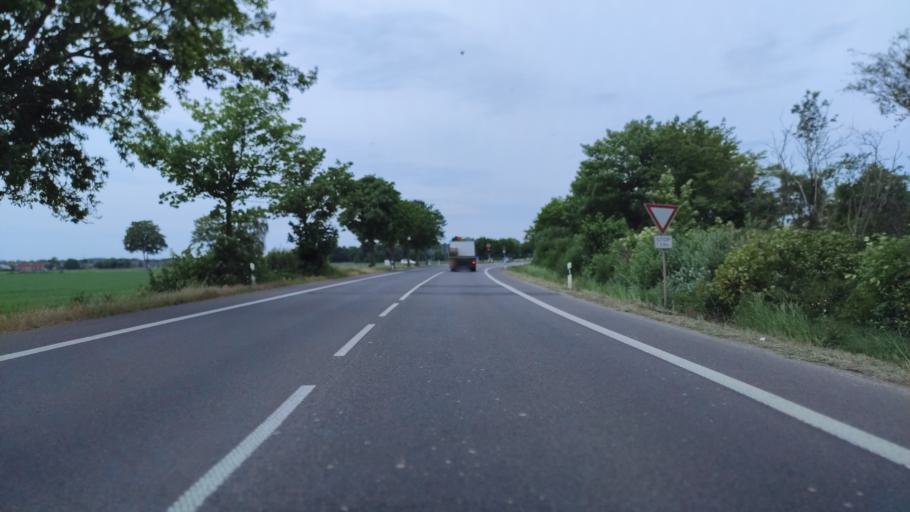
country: DE
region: North Rhine-Westphalia
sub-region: Regierungsbezirk Dusseldorf
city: Kaarst
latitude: 51.1890
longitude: 6.5750
